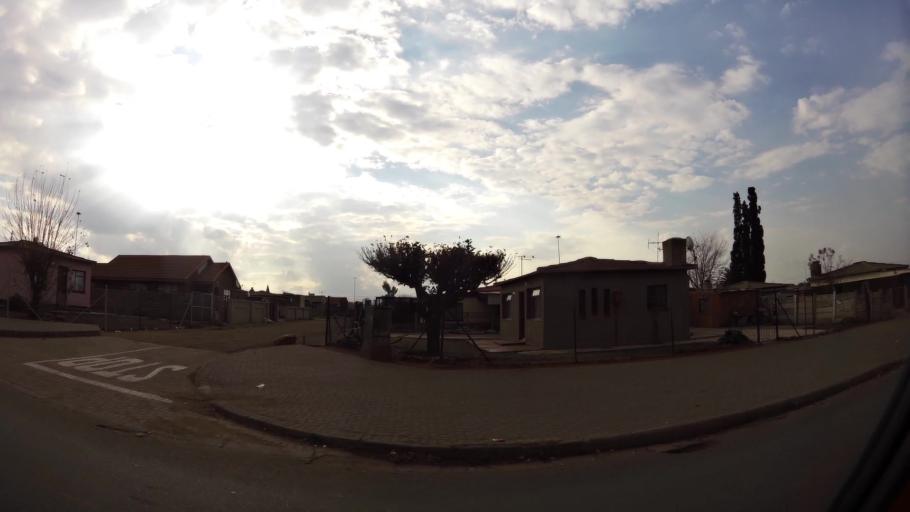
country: ZA
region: Gauteng
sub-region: Sedibeng District Municipality
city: Vereeniging
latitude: -26.6798
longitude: 27.8849
